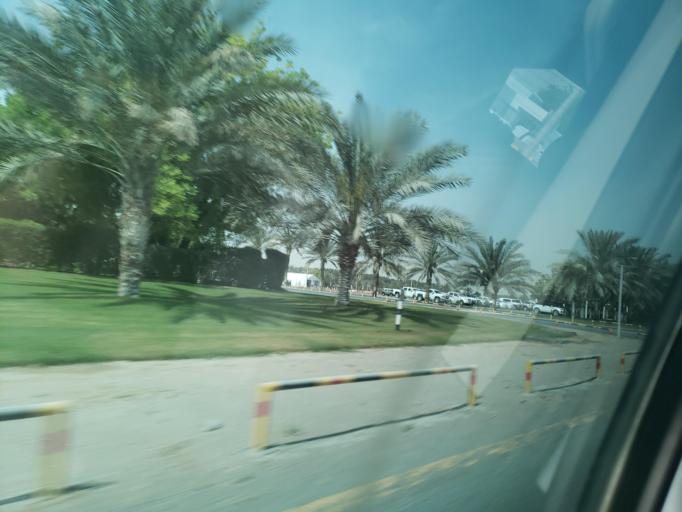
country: AE
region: Ash Shariqah
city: Sharjah
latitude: 25.3211
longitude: 55.5161
